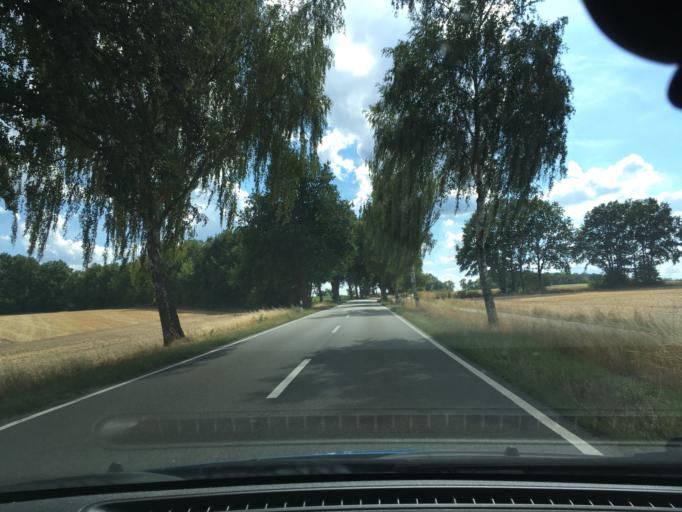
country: DE
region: Lower Saxony
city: Wriedel
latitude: 53.0108
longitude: 10.2826
